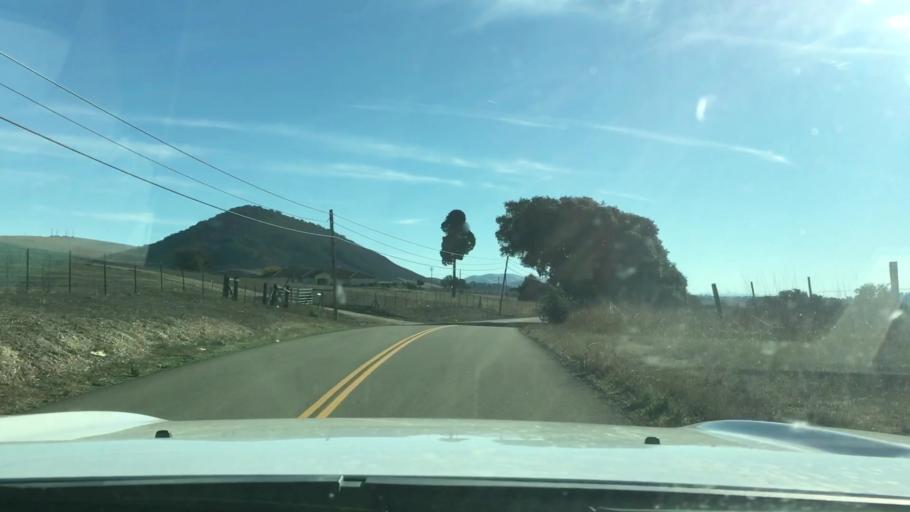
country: US
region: California
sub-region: San Luis Obispo County
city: Arroyo Grande
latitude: 35.1055
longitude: -120.5601
